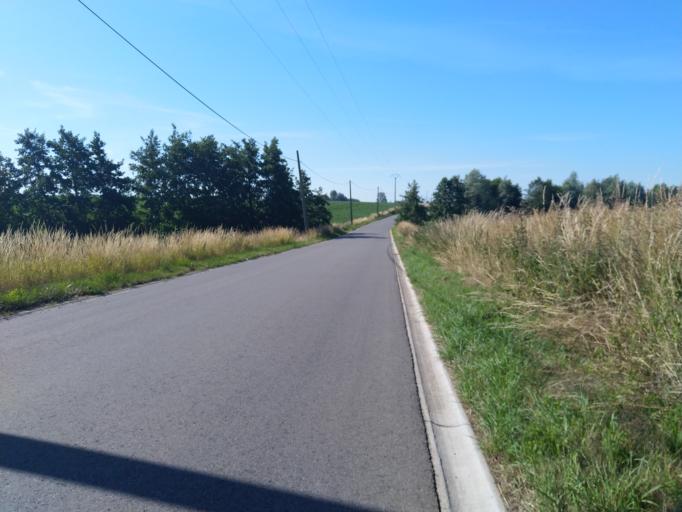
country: BE
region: Wallonia
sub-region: Province du Hainaut
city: Quevy-le-Petit
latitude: 50.3519
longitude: 3.9454
